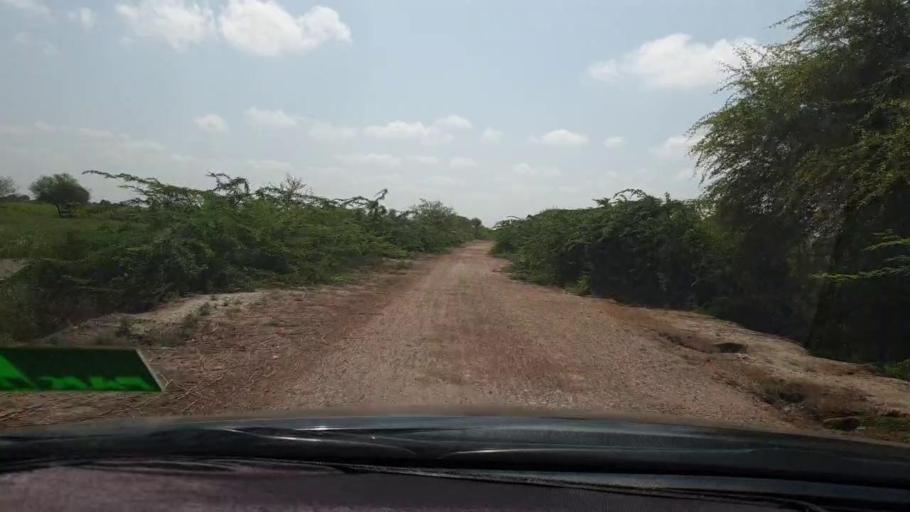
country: PK
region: Sindh
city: Tando Bago
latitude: 24.9379
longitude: 69.0935
